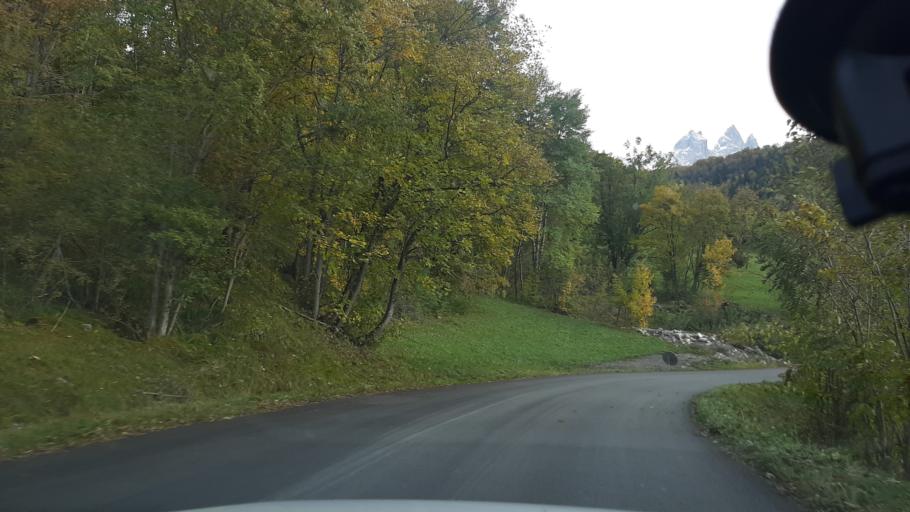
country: FR
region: Rhone-Alpes
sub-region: Departement de la Savoie
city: Villargondran
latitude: 45.1982
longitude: 6.3332
